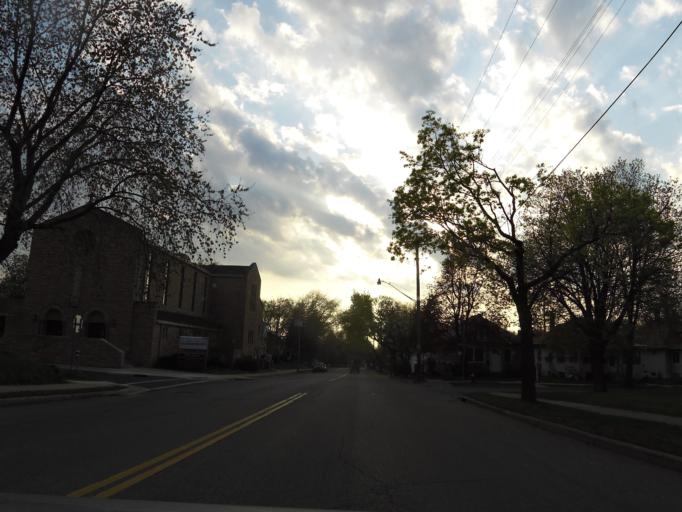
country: US
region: Minnesota
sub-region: Dakota County
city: West Saint Paul
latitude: 44.9197
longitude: -93.1042
